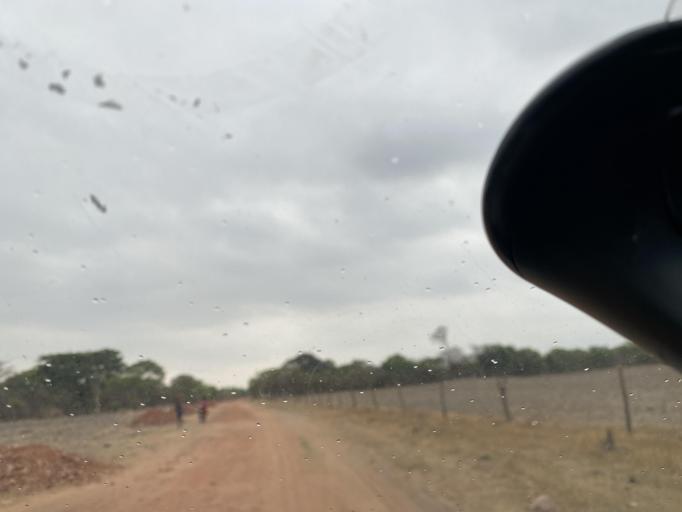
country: ZM
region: Lusaka
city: Chongwe
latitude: -15.1559
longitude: 28.7457
